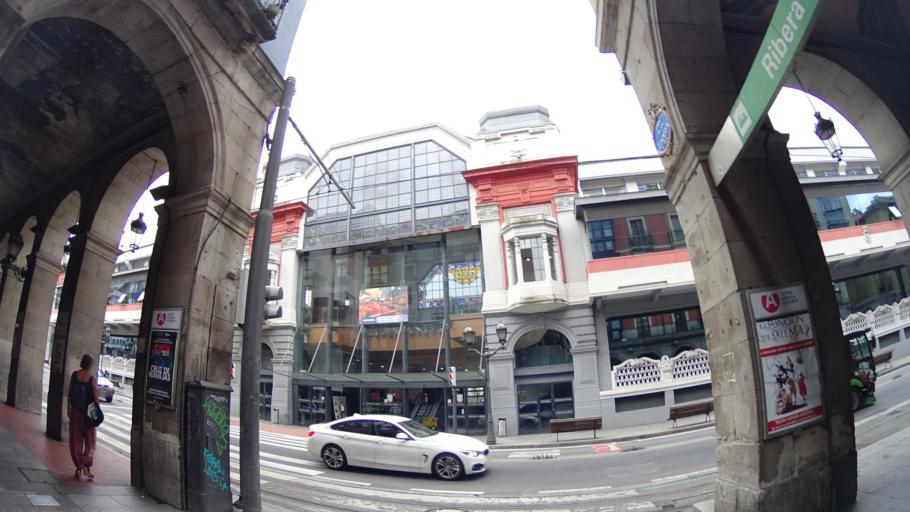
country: ES
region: Basque Country
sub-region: Bizkaia
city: Bilbao
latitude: 43.2558
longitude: -2.9241
